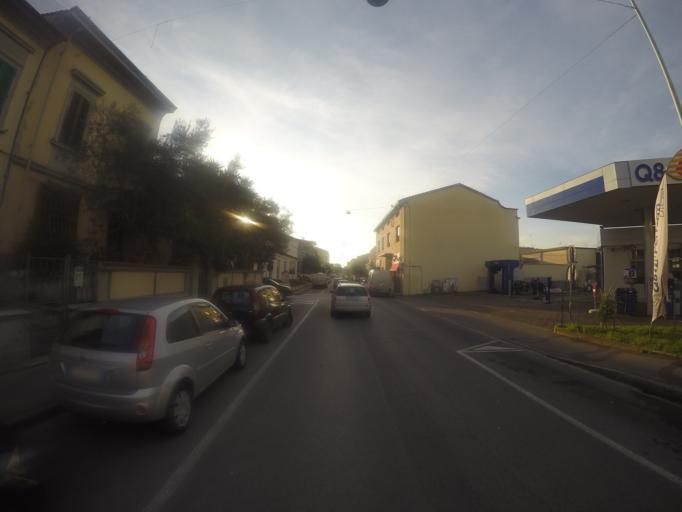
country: IT
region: Tuscany
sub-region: Provincia di Prato
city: Prato
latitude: 43.8880
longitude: 11.0811
